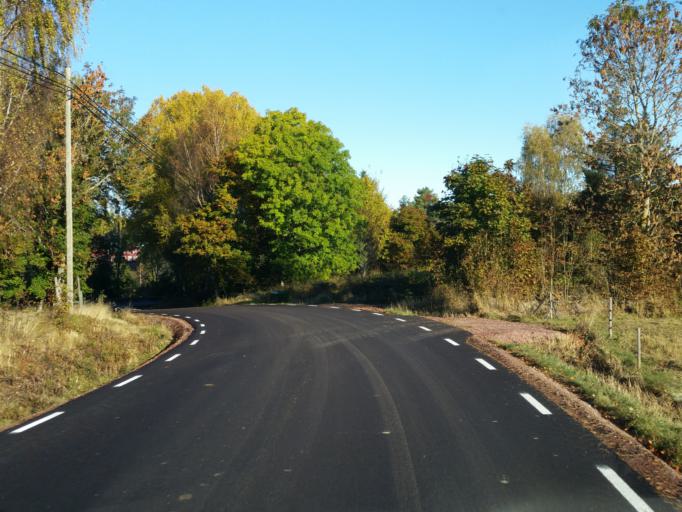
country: AX
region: Alands landsbygd
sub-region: Sund
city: Sund
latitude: 60.2233
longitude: 20.0921
